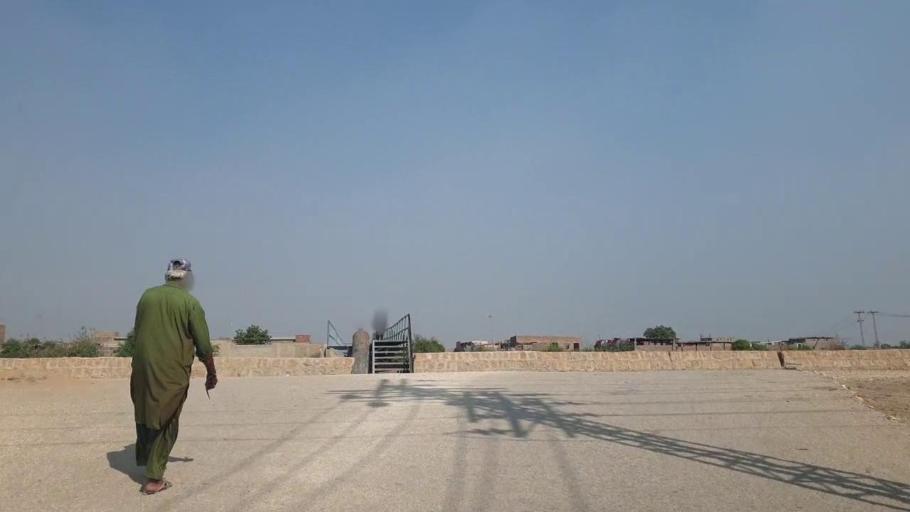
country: PK
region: Sindh
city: Hyderabad
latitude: 25.4239
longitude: 68.3570
